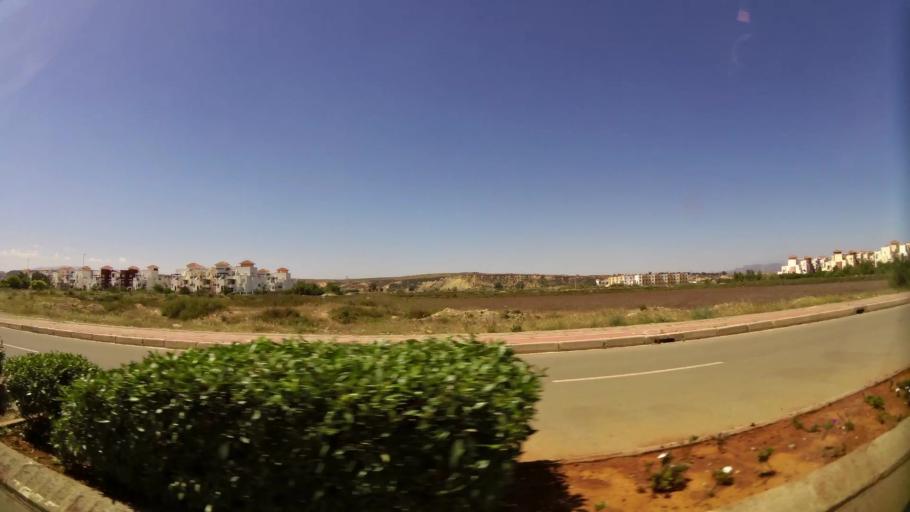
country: MA
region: Oriental
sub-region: Berkane-Taourirt
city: Madagh
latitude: 35.1041
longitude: -2.3090
